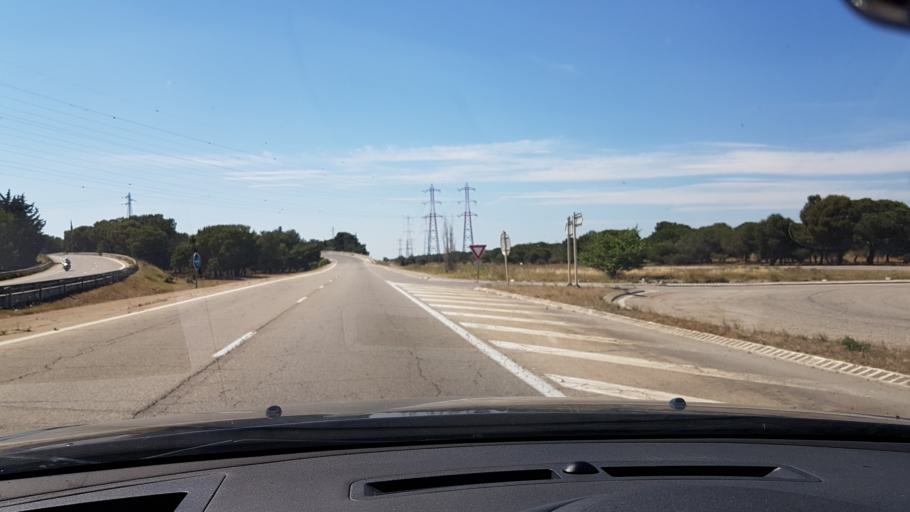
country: FR
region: Provence-Alpes-Cote d'Azur
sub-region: Departement des Bouches-du-Rhone
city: Fos-sur-Mer
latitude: 43.4769
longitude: 4.8989
